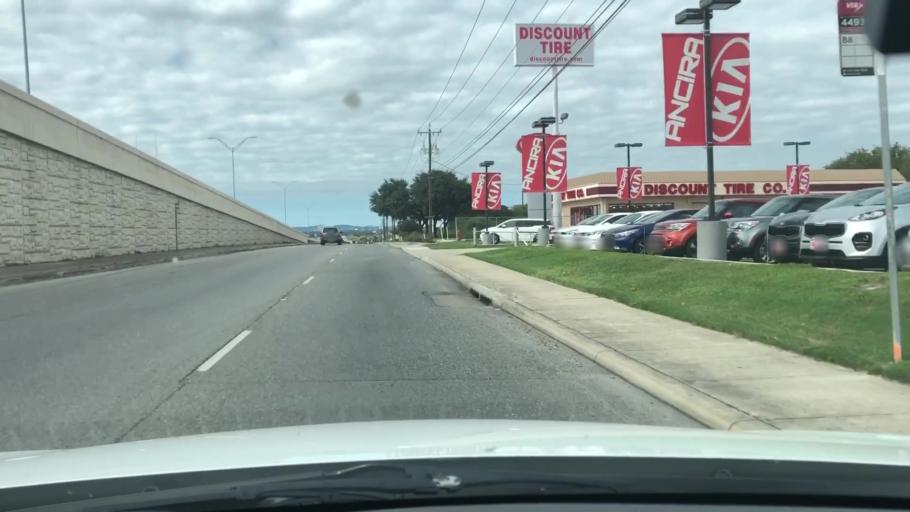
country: US
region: Texas
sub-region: Bexar County
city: Leon Valley
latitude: 29.4867
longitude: -98.6072
